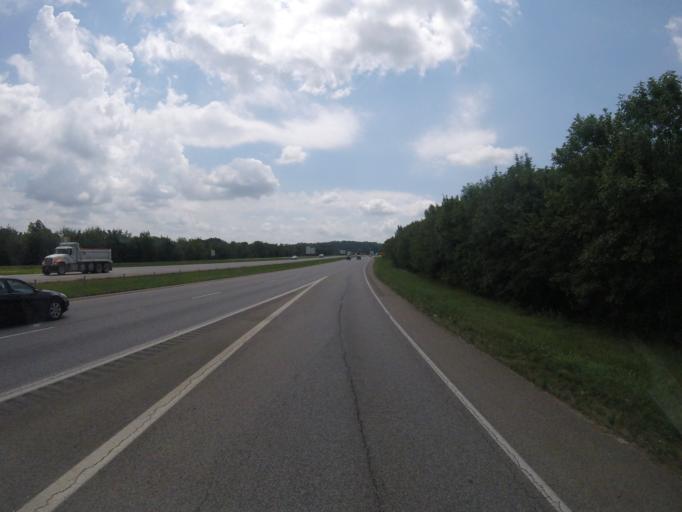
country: US
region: Arkansas
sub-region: Washington County
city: Fayetteville
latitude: 36.0510
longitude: -94.1933
